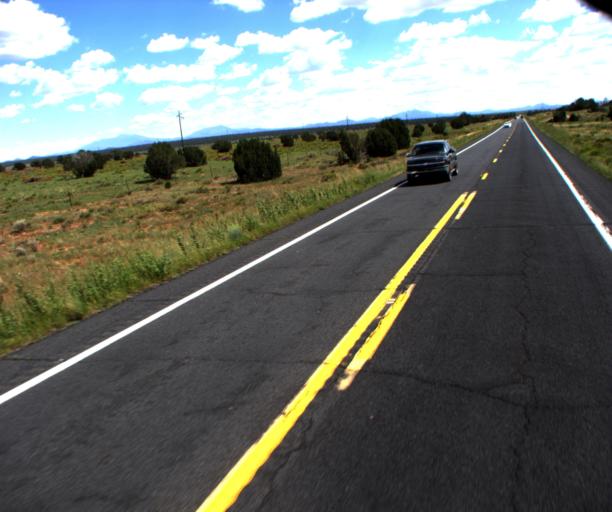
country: US
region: Arizona
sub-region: Coconino County
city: Grand Canyon Village
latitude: 35.7993
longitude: -112.1307
